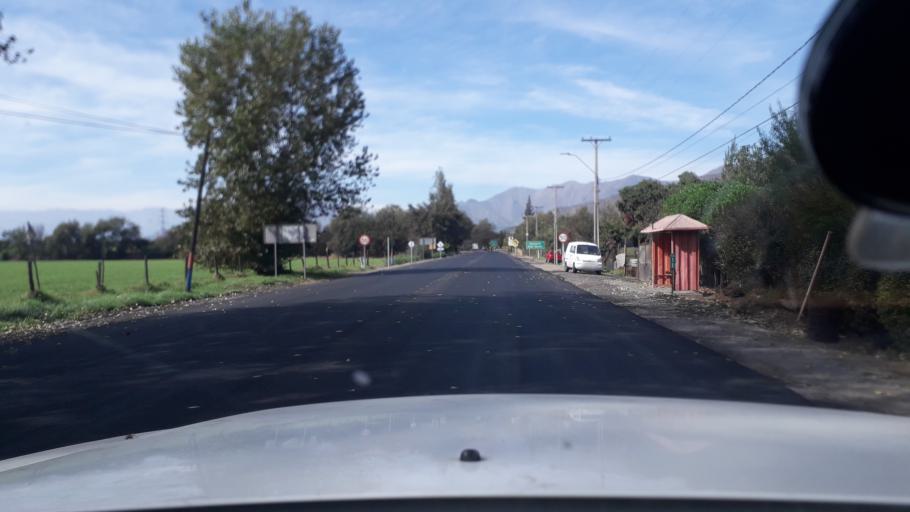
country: CL
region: Valparaiso
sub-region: Provincia de San Felipe
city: Llaillay
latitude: -32.8034
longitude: -70.9026
